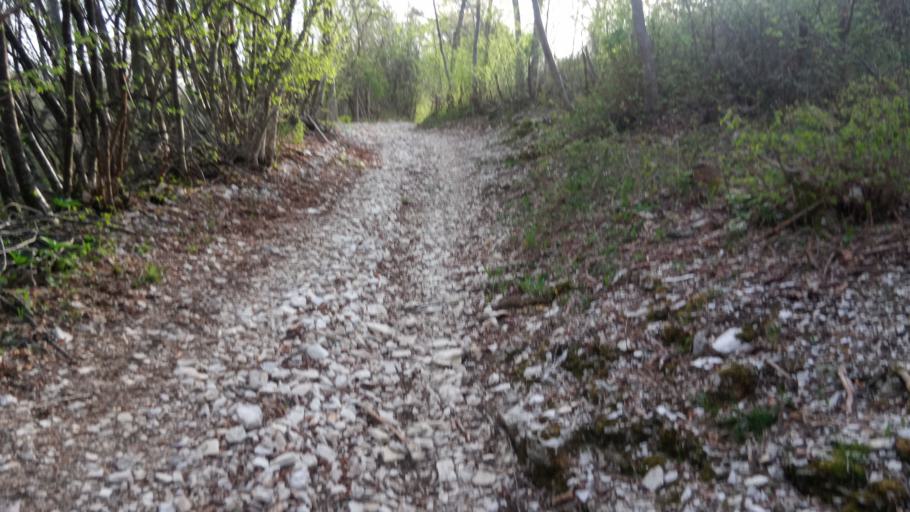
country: IT
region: Veneto
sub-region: Provincia di Vicenza
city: Conco
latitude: 45.7944
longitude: 11.6220
